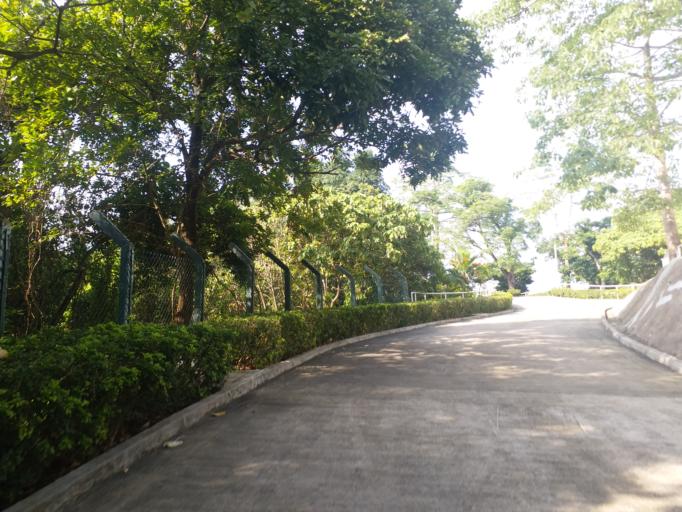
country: HK
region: Yuen Long
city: Yuen Long Kau Hui
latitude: 22.4448
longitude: 114.0099
